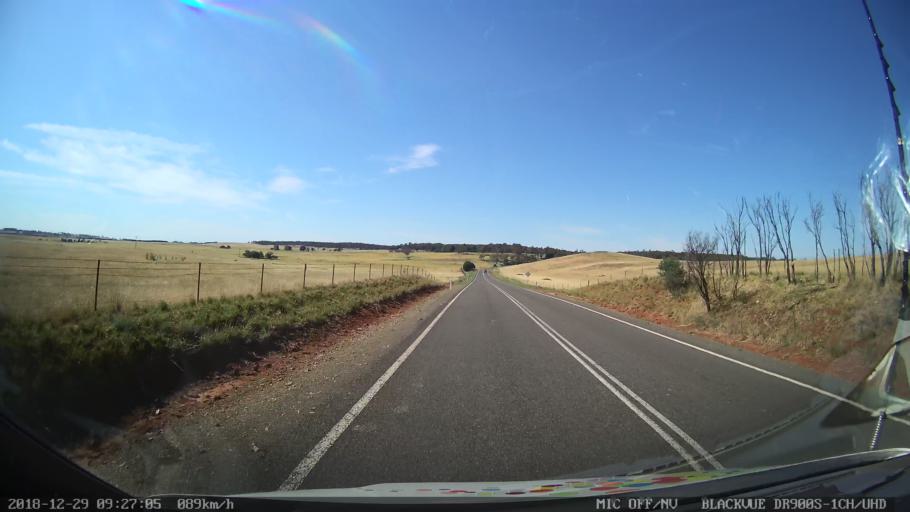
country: AU
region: New South Wales
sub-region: Upper Lachlan Shire
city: Crookwell
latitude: -34.5619
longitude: 149.3858
